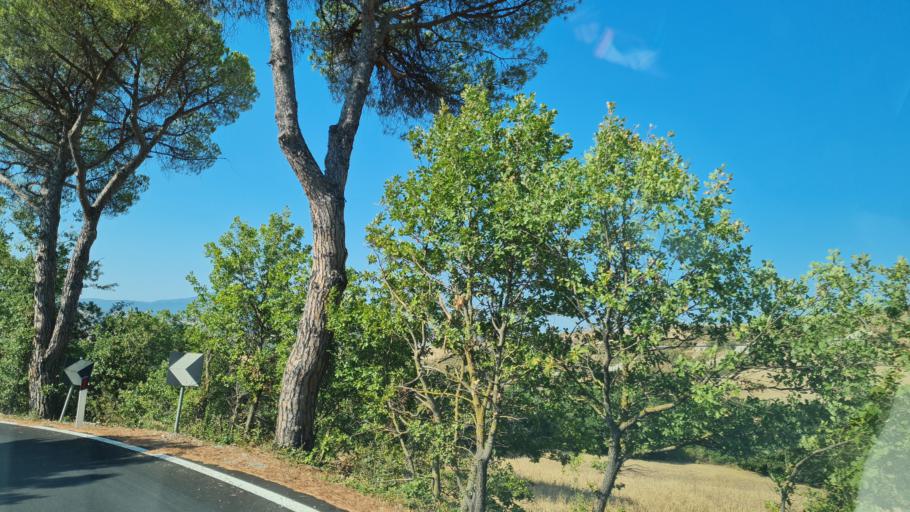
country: IT
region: Tuscany
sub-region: Provincia di Siena
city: Chianciano Terme
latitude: 43.0231
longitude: 11.7693
